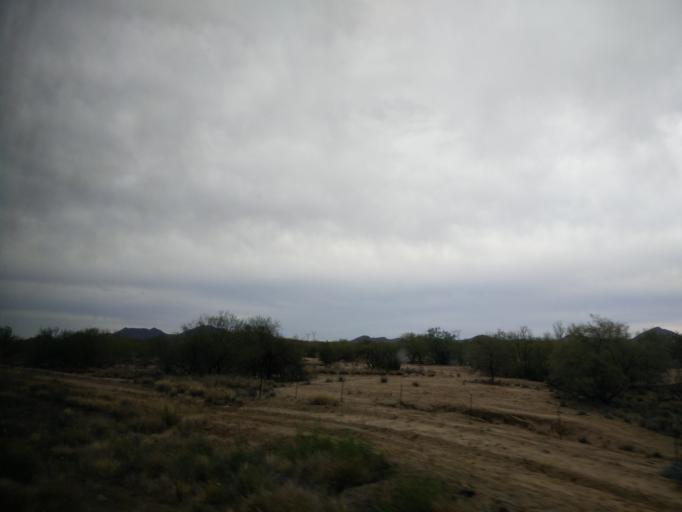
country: MX
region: Sonora
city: Hermosillo
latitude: 28.7366
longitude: -110.9767
